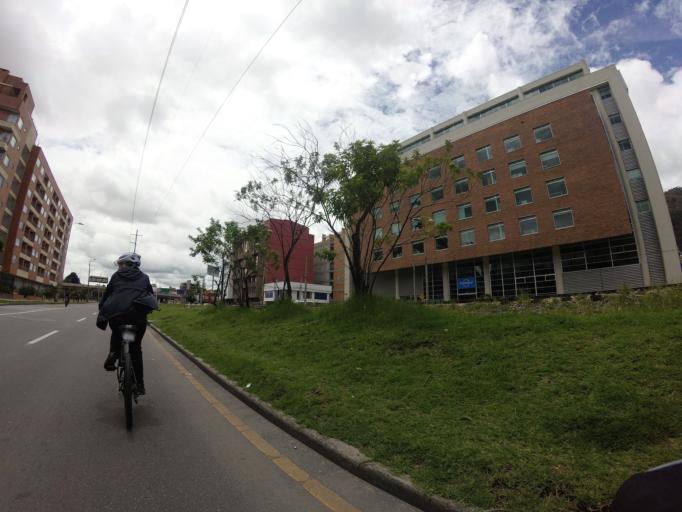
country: CO
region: Bogota D.C.
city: Barrio San Luis
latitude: 4.7015
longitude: -74.0330
